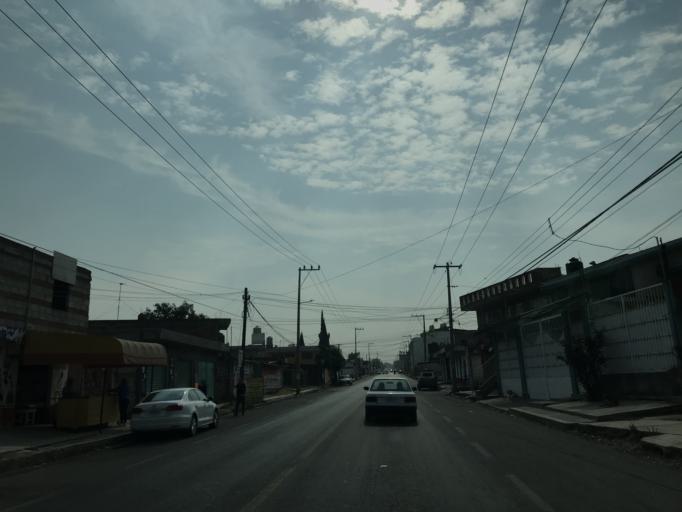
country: MX
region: Tlaxcala
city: Tenancingo
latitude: 19.1508
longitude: -98.2196
